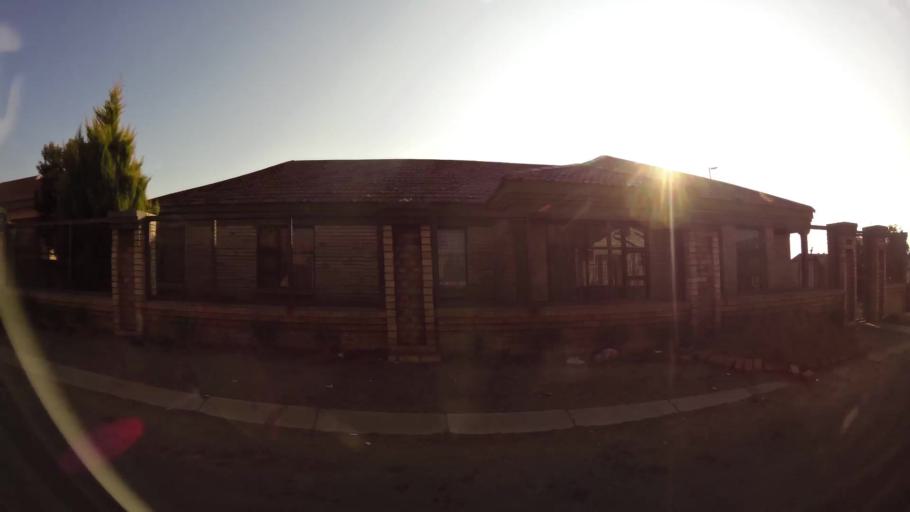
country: ZA
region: Orange Free State
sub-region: Mangaung Metropolitan Municipality
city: Bloemfontein
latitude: -29.1603
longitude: 26.2081
